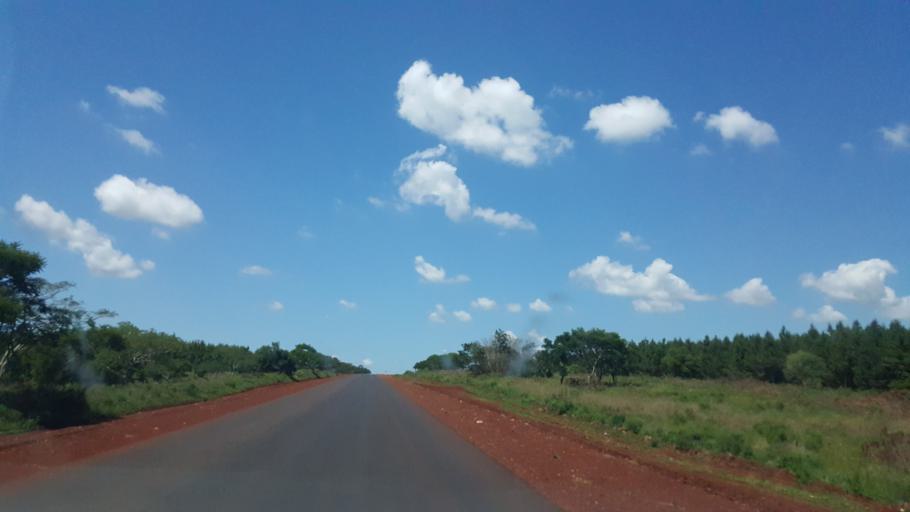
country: AR
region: Corrientes
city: Santo Tome
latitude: -28.4906
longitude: -56.0445
